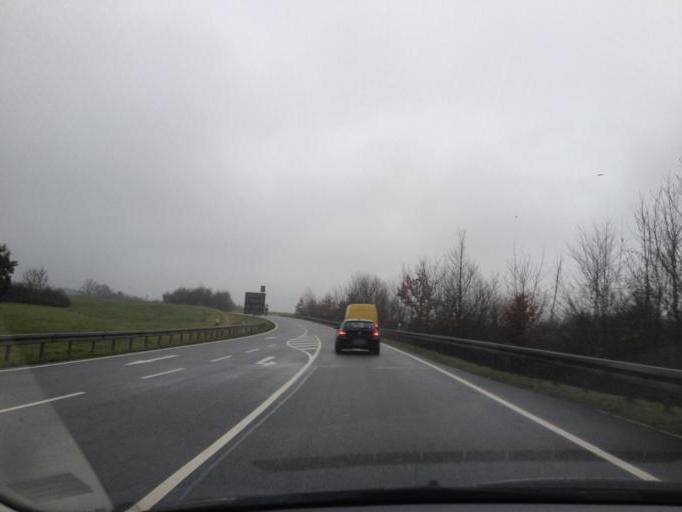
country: DE
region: Bavaria
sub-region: Regierungsbezirk Mittelfranken
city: Heroldsberg
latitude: 49.5436
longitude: 11.1631
